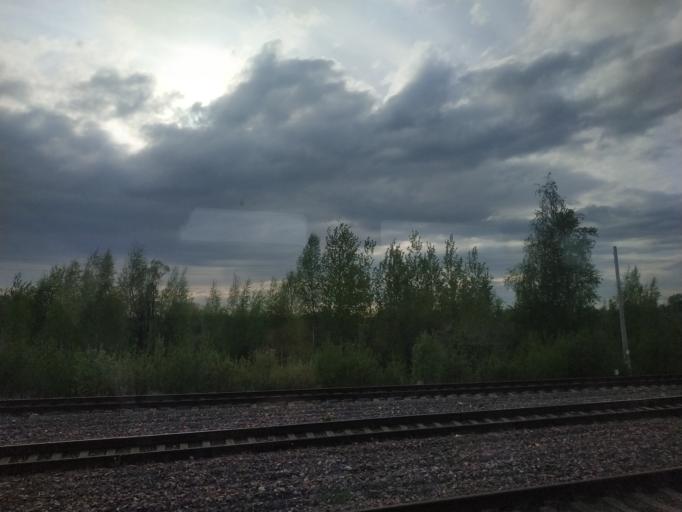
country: RU
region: Smolensk
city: Ugra
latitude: 54.7757
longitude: 34.3426
